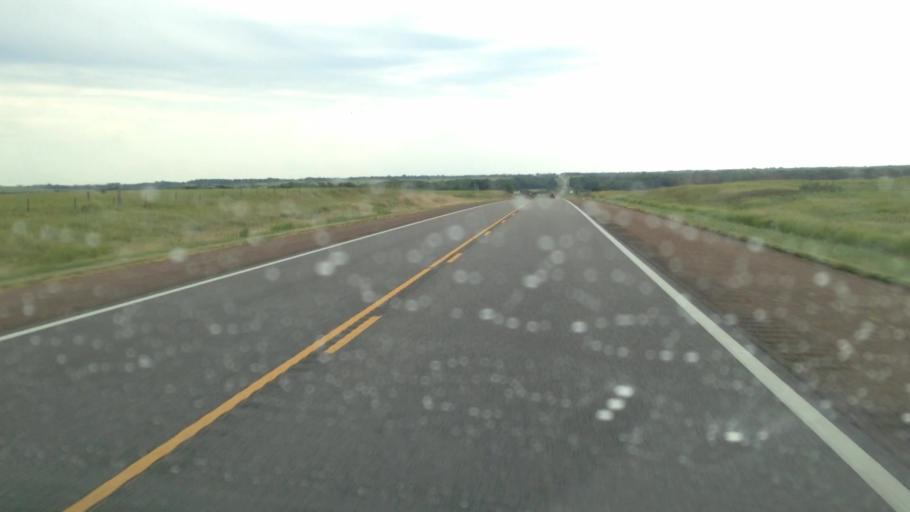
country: US
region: Kansas
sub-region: Coffey County
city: Burlington
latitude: 38.0458
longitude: -95.7390
